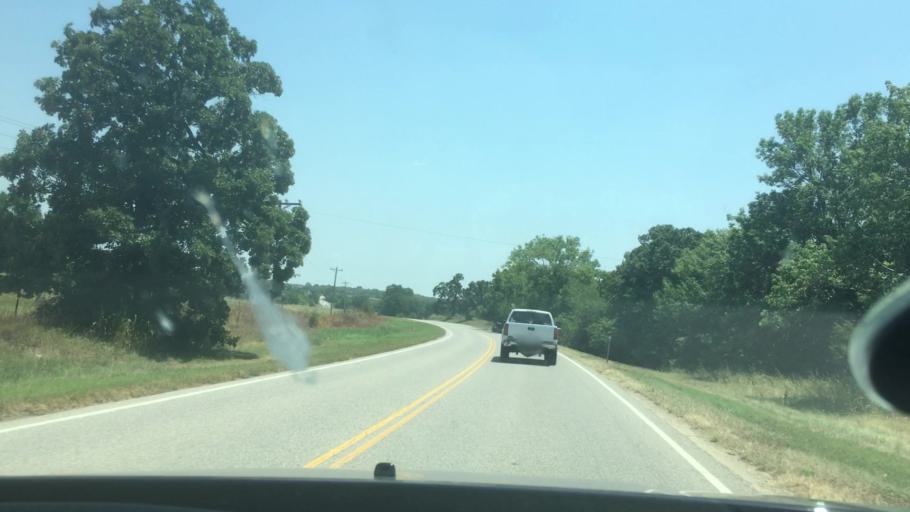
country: US
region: Oklahoma
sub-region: Bryan County
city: Durant
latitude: 34.1749
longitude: -96.4146
